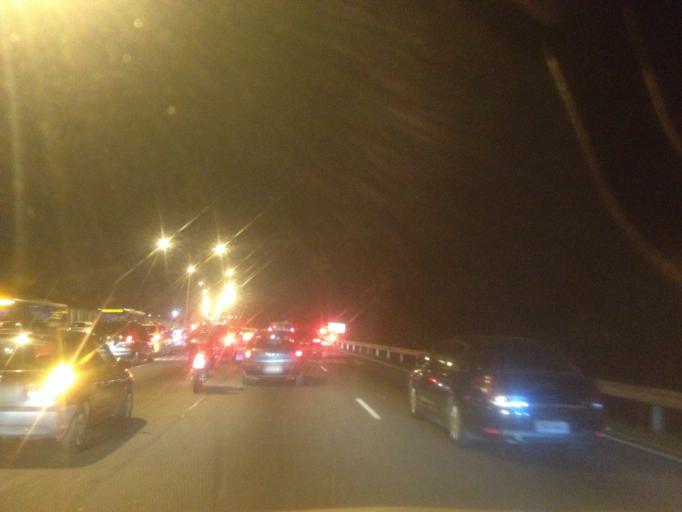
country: BR
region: Rio de Janeiro
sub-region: Rio De Janeiro
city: Rio de Janeiro
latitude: -22.8564
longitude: -43.2382
